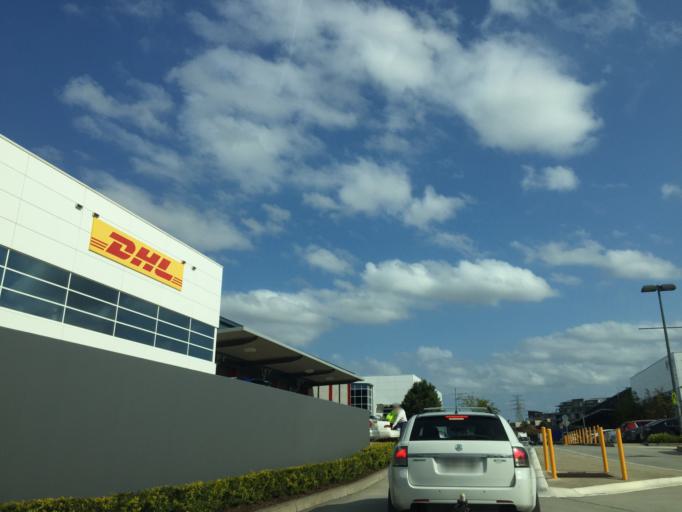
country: AU
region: New South Wales
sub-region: Strathfield
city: Homebush
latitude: -33.8588
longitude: 151.0644
